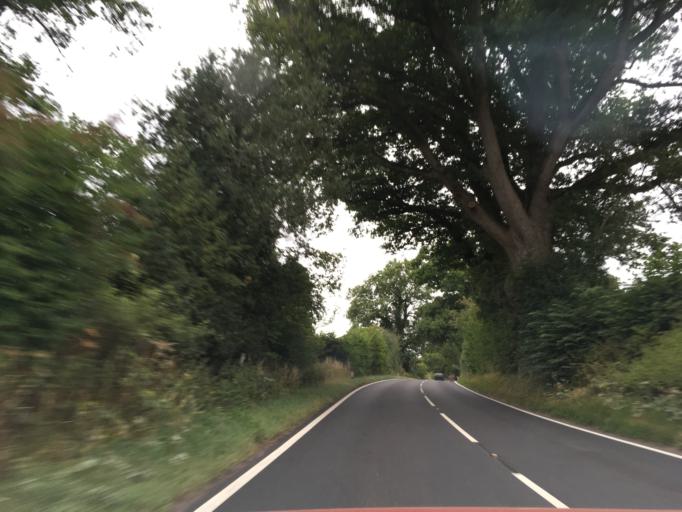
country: GB
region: Wales
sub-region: Sir Powys
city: Brecon
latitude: 51.9155
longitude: -3.2966
